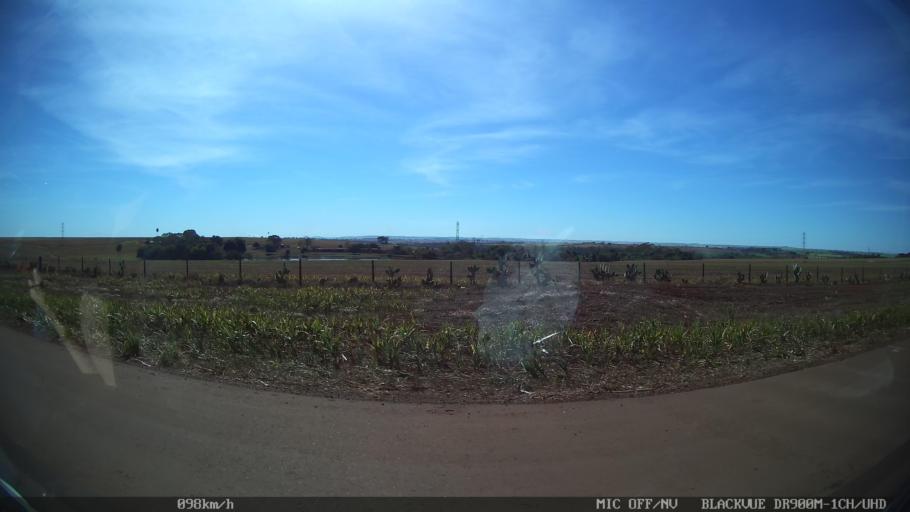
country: BR
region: Sao Paulo
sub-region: Sao Joaquim Da Barra
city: Sao Joaquim da Barra
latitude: -20.5208
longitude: -47.8633
